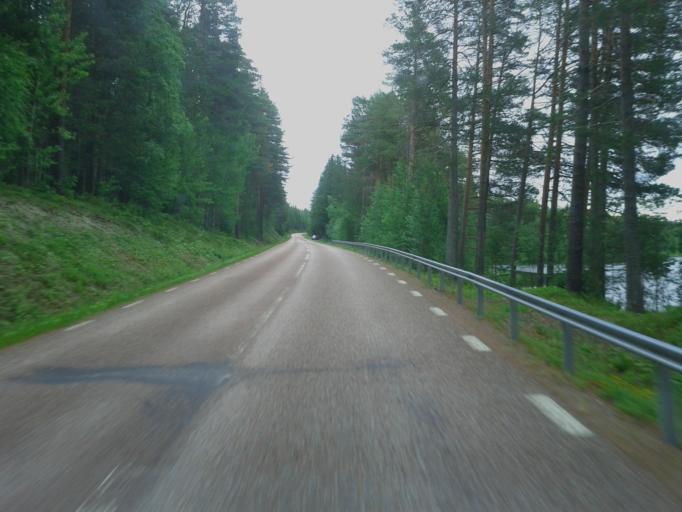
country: NO
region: Hedmark
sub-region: Trysil
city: Innbygda
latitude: 61.8362
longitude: 12.8187
